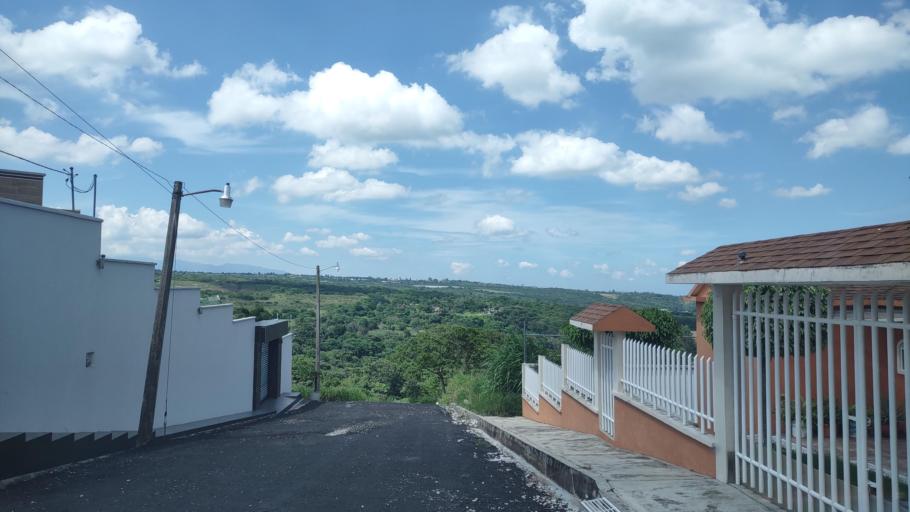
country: MX
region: Veracruz
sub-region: Emiliano Zapata
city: Dos Rios
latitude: 19.4937
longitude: -96.8156
